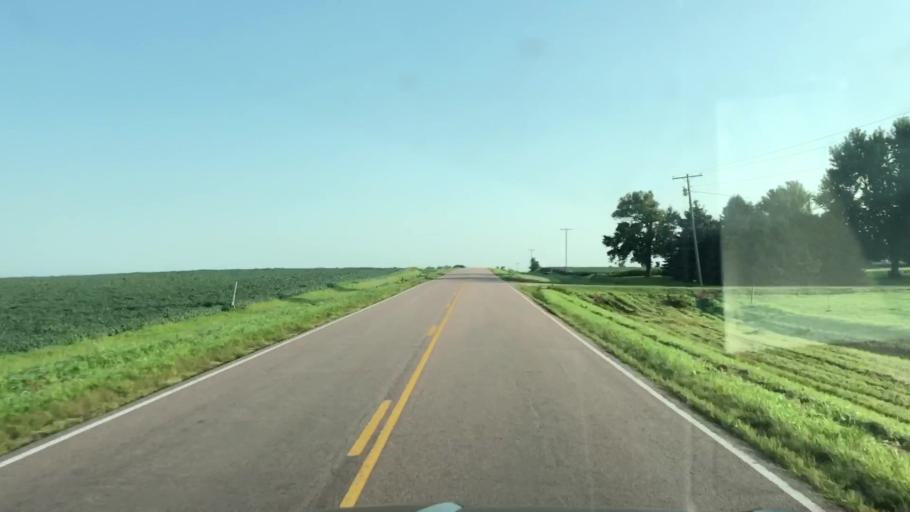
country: US
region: Iowa
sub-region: Lyon County
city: George
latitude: 43.2666
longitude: -95.9999
